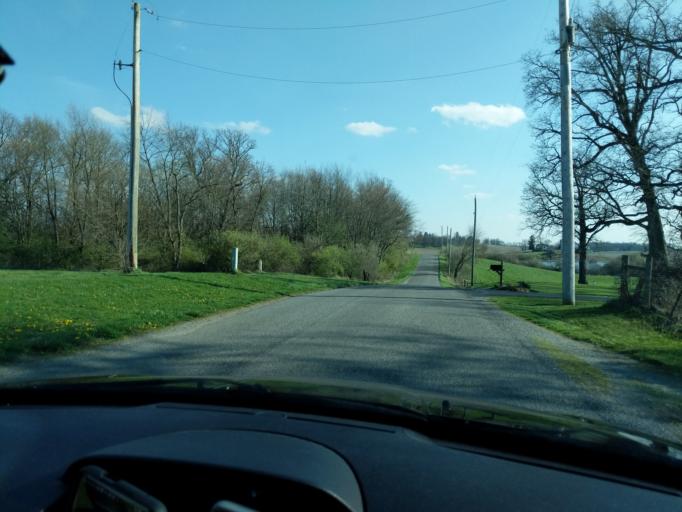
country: US
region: Ohio
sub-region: Champaign County
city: Urbana
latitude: 40.0816
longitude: -83.6663
